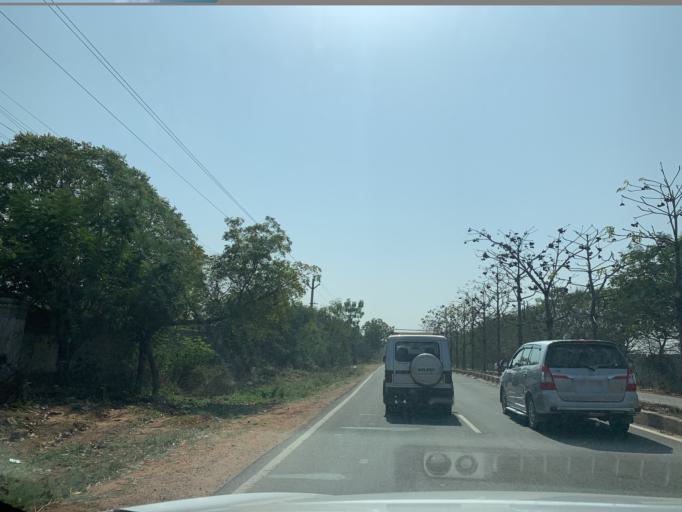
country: IN
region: Telangana
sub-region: Rangareddi
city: Sriramnagar
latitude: 17.3376
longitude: 78.3044
